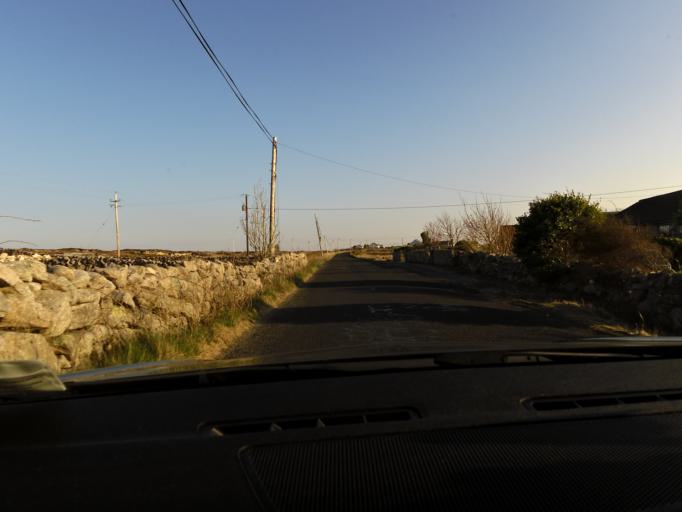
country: IE
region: Connaught
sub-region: County Galway
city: Oughterard
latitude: 53.2580
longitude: -9.5434
